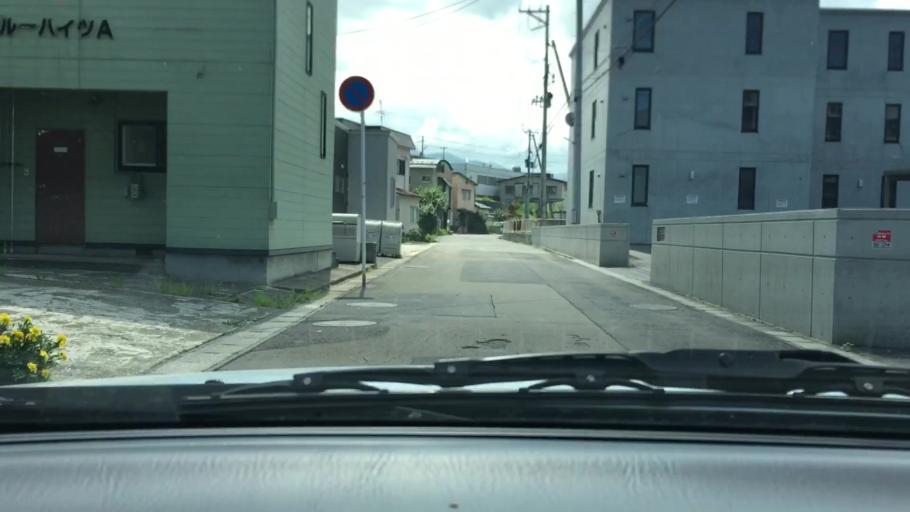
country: JP
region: Aomori
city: Hirosaki
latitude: 40.5875
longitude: 140.4676
